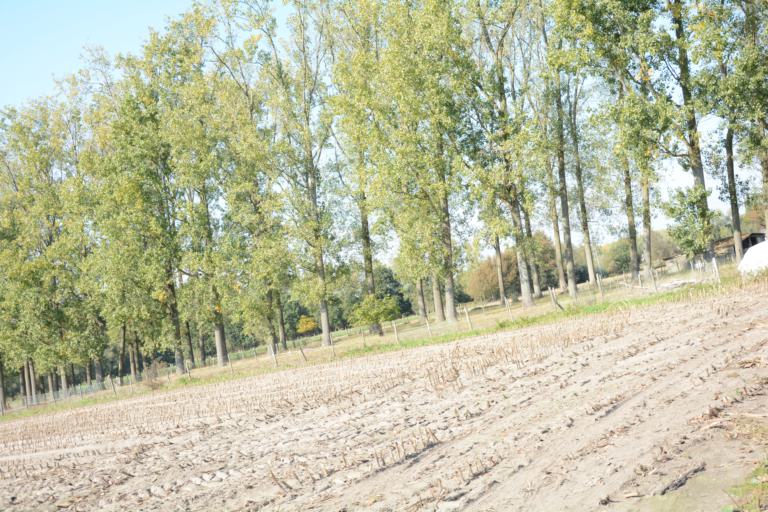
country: BE
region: Flanders
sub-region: Provincie Oost-Vlaanderen
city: Buggenhout
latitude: 51.0203
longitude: 4.2406
